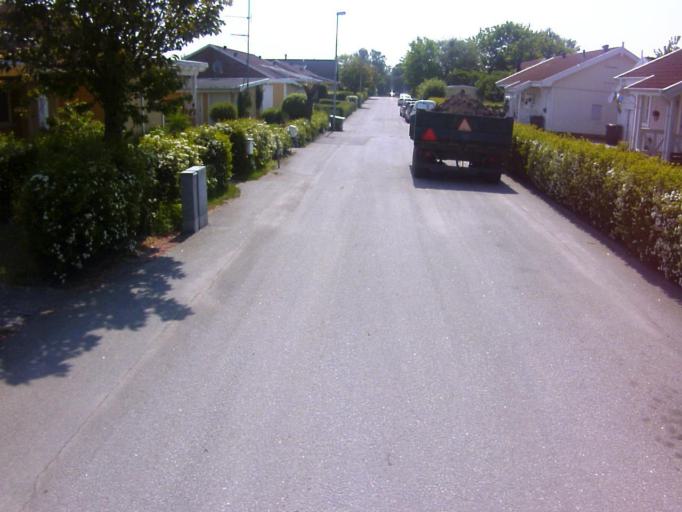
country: SE
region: Blekinge
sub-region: Karlshamns Kommun
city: Morrum
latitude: 56.1284
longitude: 14.6696
